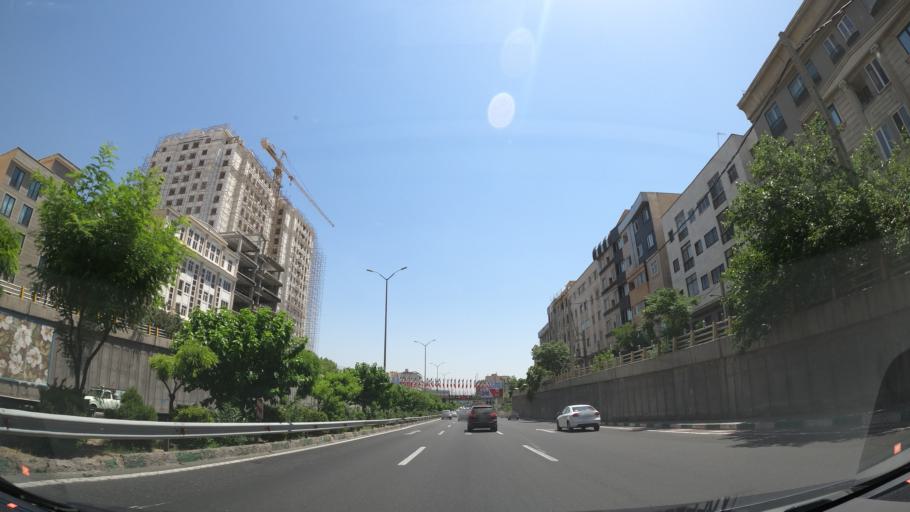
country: IR
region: Tehran
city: Tajrish
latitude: 35.7759
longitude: 51.3719
